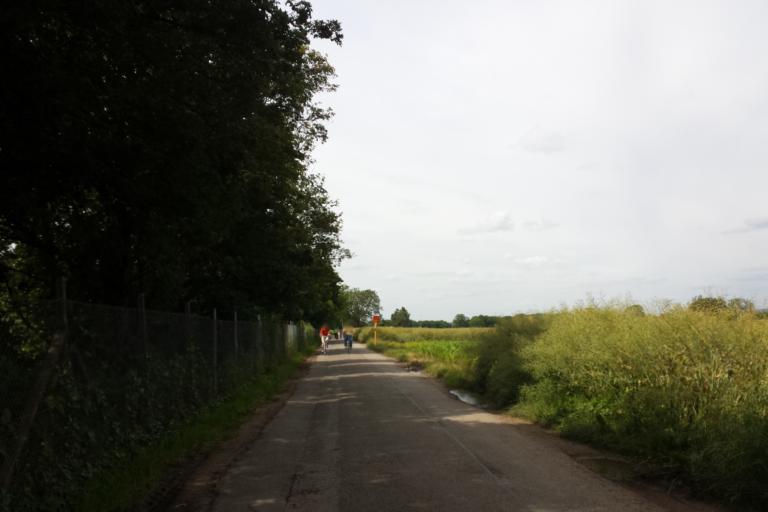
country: DE
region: Baden-Wuerttemberg
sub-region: Karlsruhe Region
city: Dossenheim
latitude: 49.4348
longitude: 8.6543
